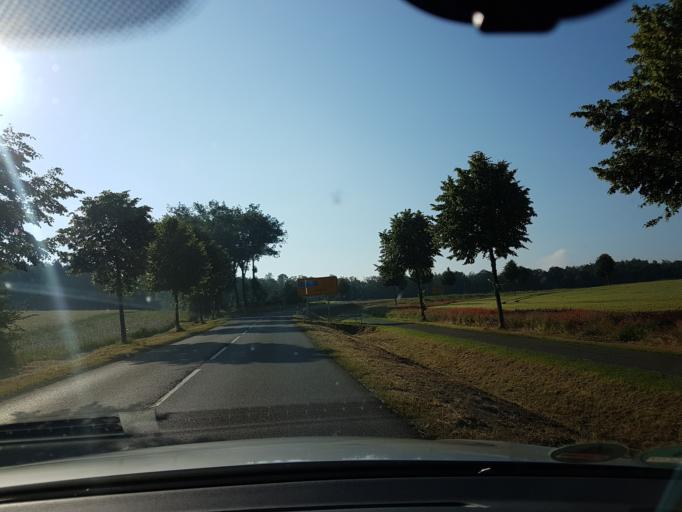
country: DE
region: Saxony-Anhalt
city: Harbke
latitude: 52.2167
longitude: 11.0409
